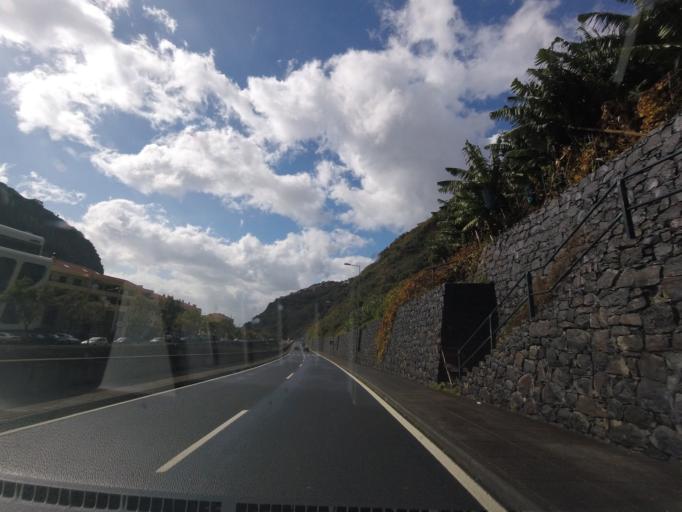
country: PT
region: Madeira
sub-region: Ribeira Brava
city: Campanario
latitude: 32.6802
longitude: -17.0603
